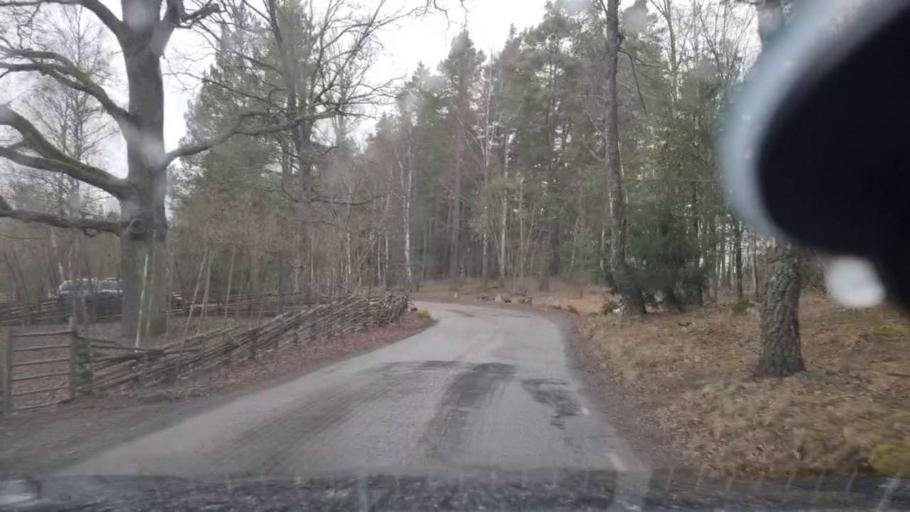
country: SE
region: Stockholm
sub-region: Taby Kommun
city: Taby
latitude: 59.4898
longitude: 18.0058
